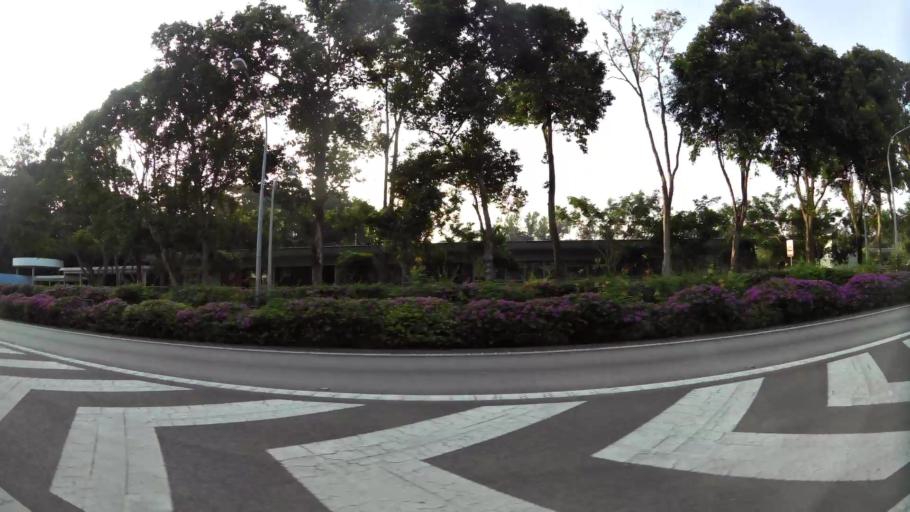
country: SG
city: Singapore
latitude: 1.3004
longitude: 103.9072
